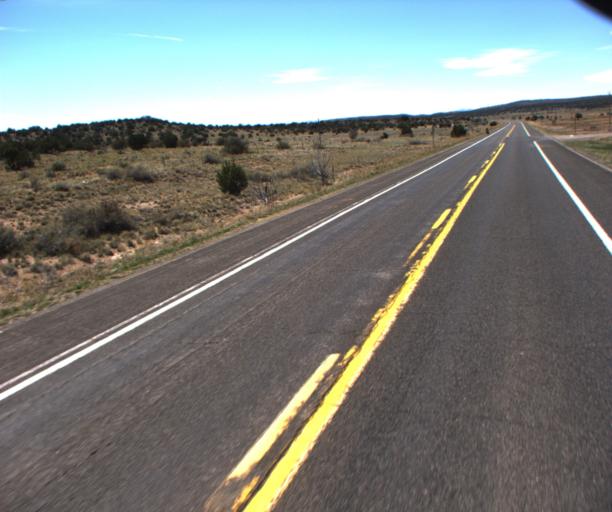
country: US
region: Arizona
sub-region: Mohave County
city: Peach Springs
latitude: 35.5517
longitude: -113.3112
